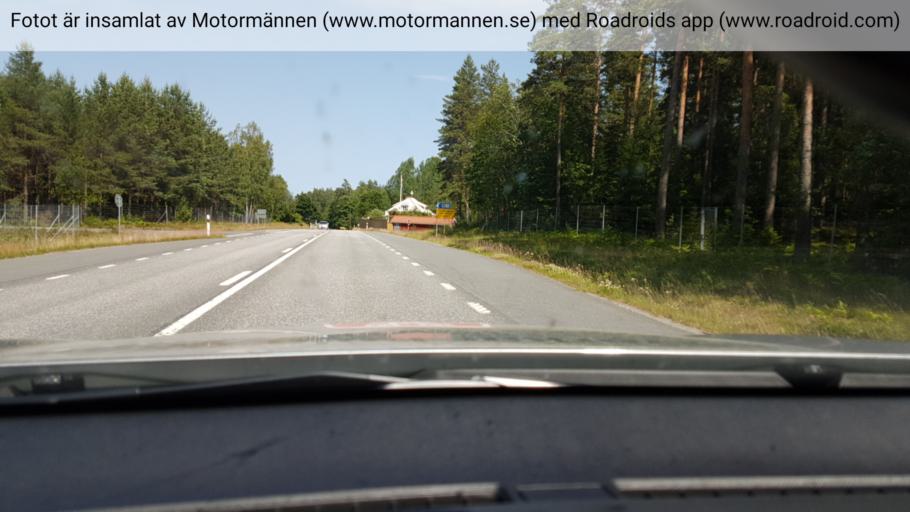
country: SE
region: Joenkoeping
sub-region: Eksjo Kommun
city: Eksjoe
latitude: 57.6370
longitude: 14.9118
